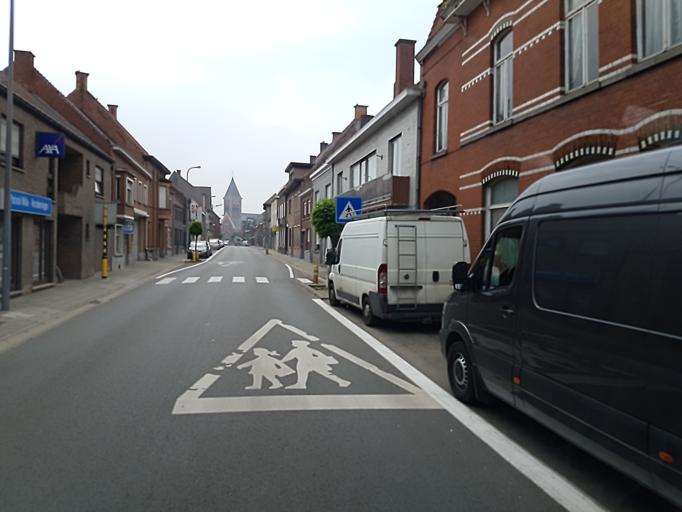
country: BE
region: Flanders
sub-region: Provincie West-Vlaanderen
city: Dentergem
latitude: 50.9329
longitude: 3.3972
